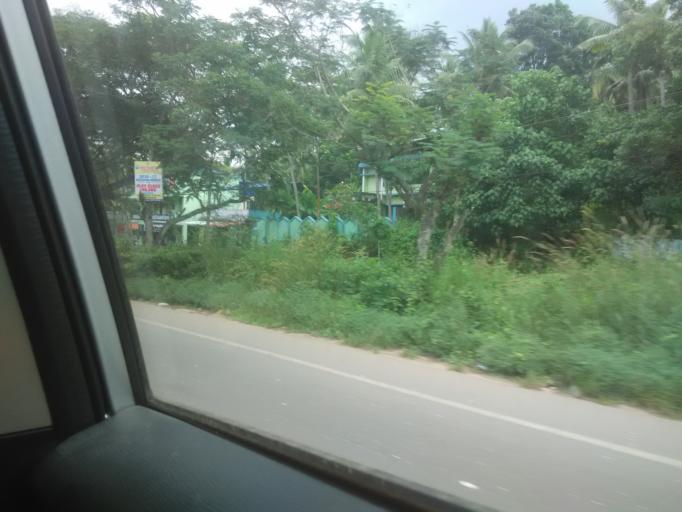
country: IN
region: Kerala
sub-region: Thiruvananthapuram
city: Attingal
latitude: 8.6343
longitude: 76.8463
